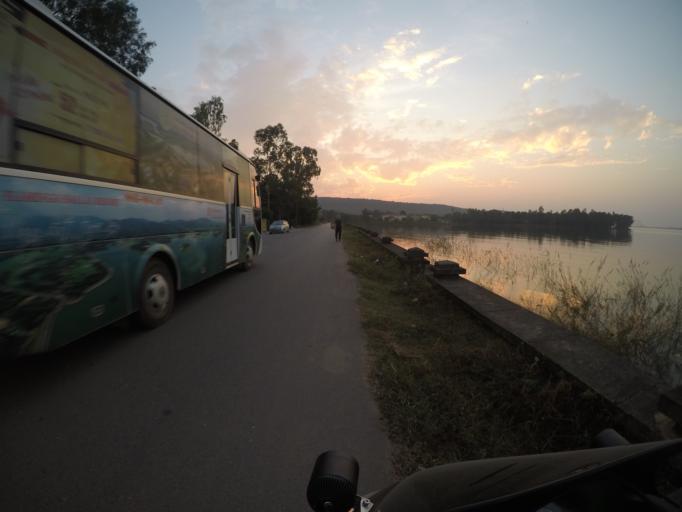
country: VN
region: Vinh Phuc
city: Phuc Yen
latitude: 21.3127
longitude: 105.7255
